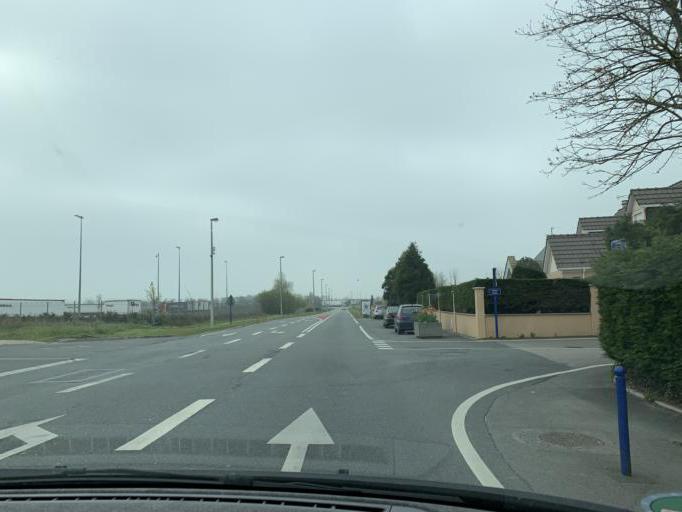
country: FR
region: Nord-Pas-de-Calais
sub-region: Departement du Pas-de-Calais
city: Marck
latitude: 50.9447
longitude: 1.9399
